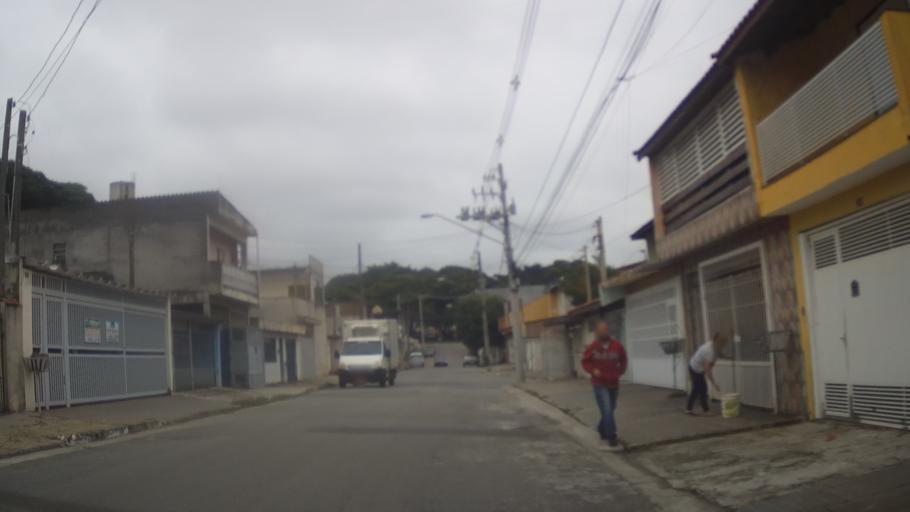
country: BR
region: Sao Paulo
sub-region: Guarulhos
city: Guarulhos
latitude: -23.4344
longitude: -46.5107
